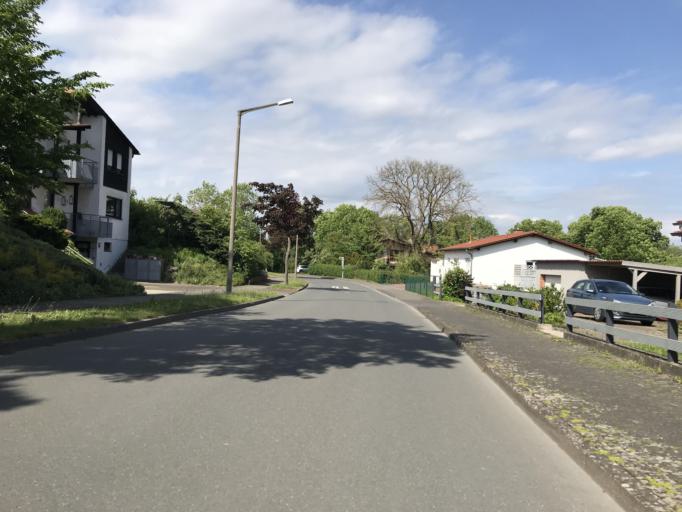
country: DE
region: Hesse
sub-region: Regierungsbezirk Kassel
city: Wolfhagen
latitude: 51.3268
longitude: 9.1635
